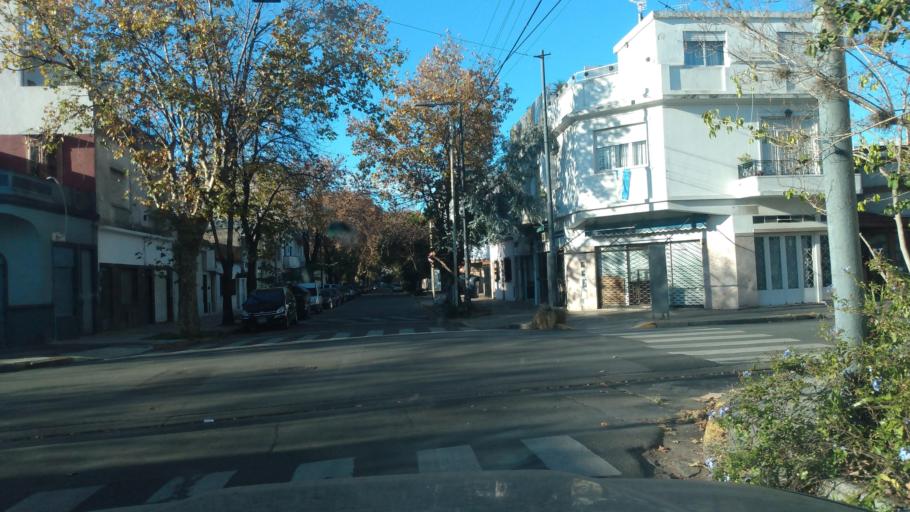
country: AR
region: Buenos Aires F.D.
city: Villa Santa Rita
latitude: -34.5843
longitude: -58.4827
